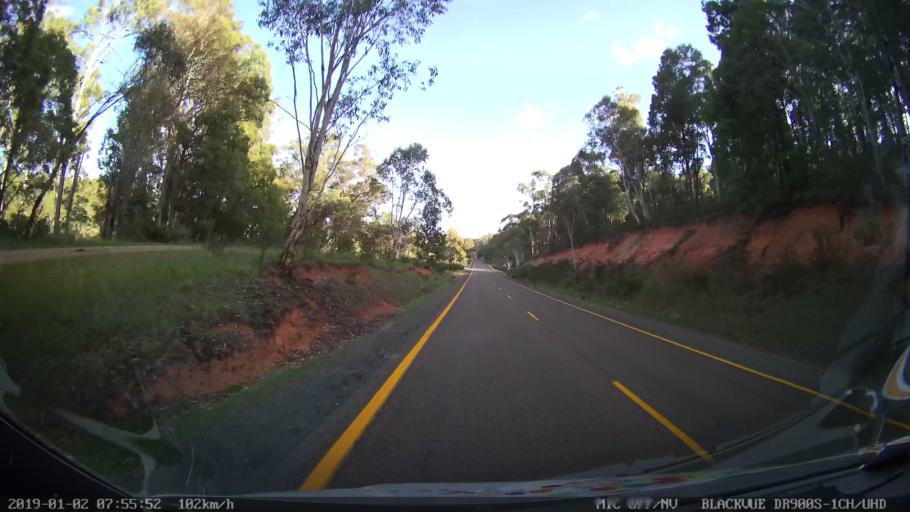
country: AU
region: New South Wales
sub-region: Tumut Shire
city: Tumut
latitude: -35.6782
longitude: 148.4863
